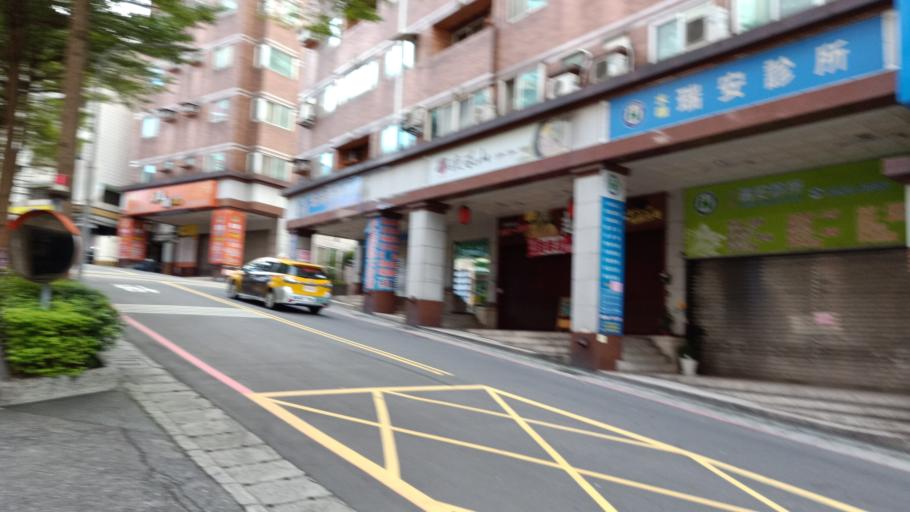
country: TW
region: Taipei
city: Taipei
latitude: 25.1775
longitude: 121.4477
